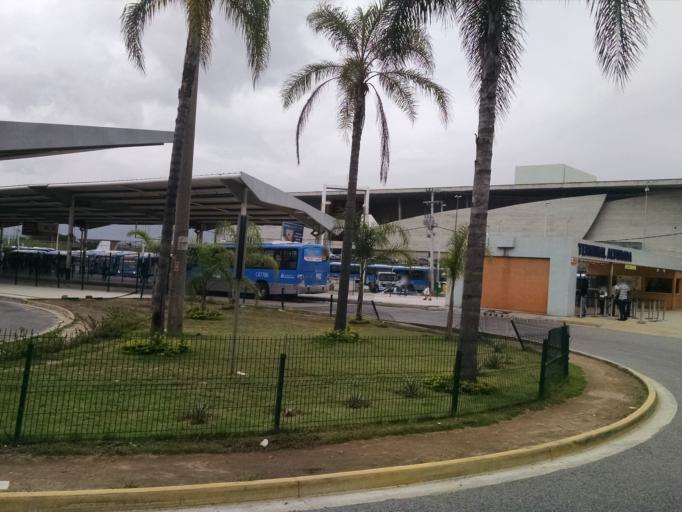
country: BR
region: Rio de Janeiro
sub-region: Rio De Janeiro
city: Rio de Janeiro
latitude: -23.0015
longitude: -43.3643
